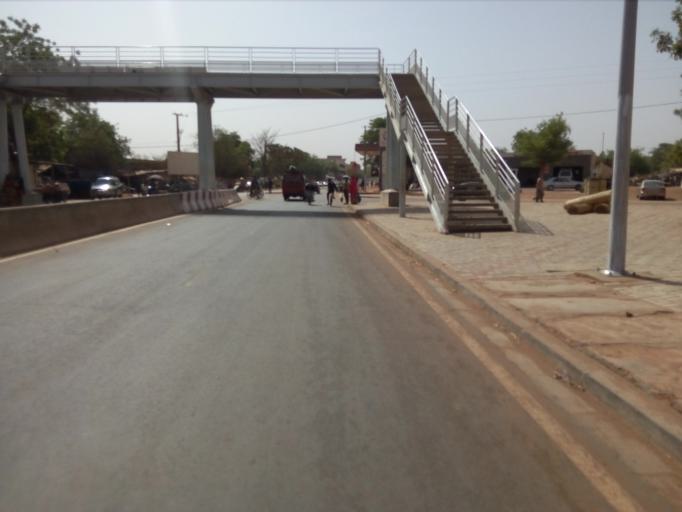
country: NE
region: Niamey
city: Niamey
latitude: 13.5205
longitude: 2.1213
